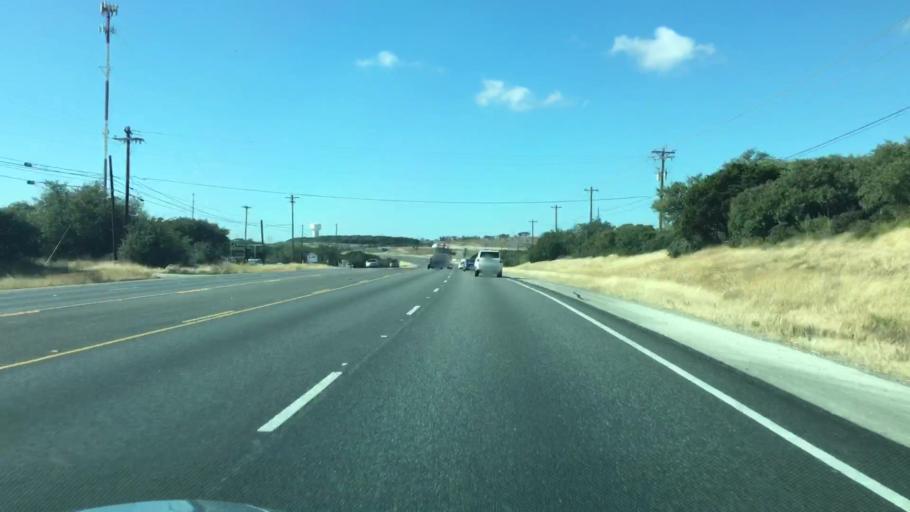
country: US
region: Texas
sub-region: Hays County
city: Dripping Springs
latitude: 30.1948
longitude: -98.0535
